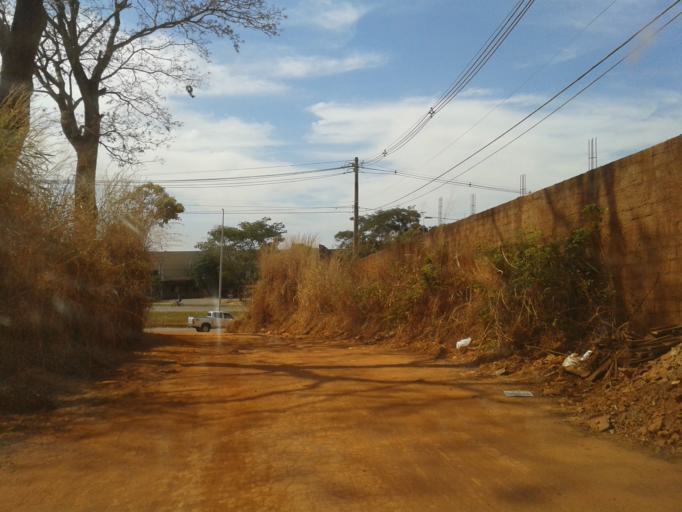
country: BR
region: Goias
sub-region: Goiania
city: Goiania
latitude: -16.6410
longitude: -49.3425
